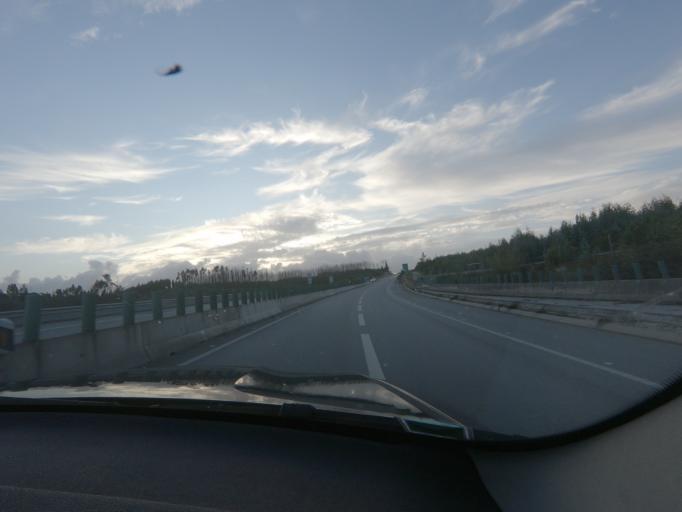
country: PT
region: Viseu
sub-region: Mortagua
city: Mortagua
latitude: 40.3490
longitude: -8.1864
